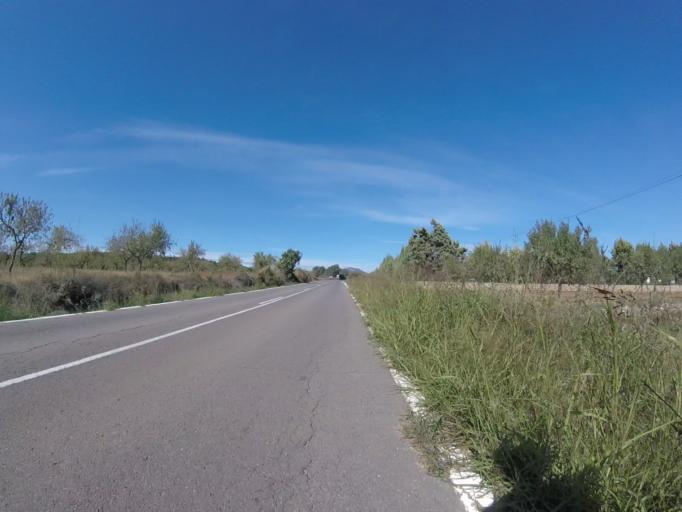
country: ES
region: Valencia
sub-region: Provincia de Castello
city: Benlloch
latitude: 40.2192
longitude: 0.0158
